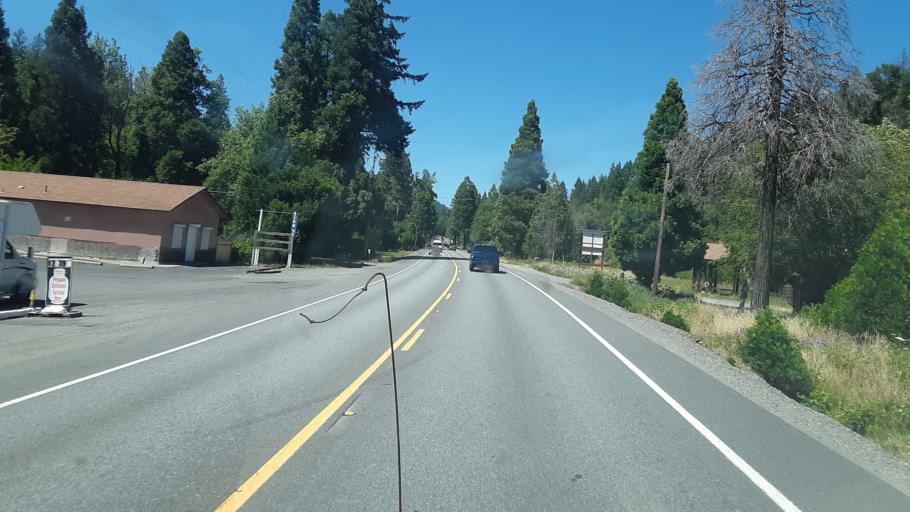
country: US
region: Oregon
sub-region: Josephine County
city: Cave Junction
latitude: 42.2892
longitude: -123.6125
